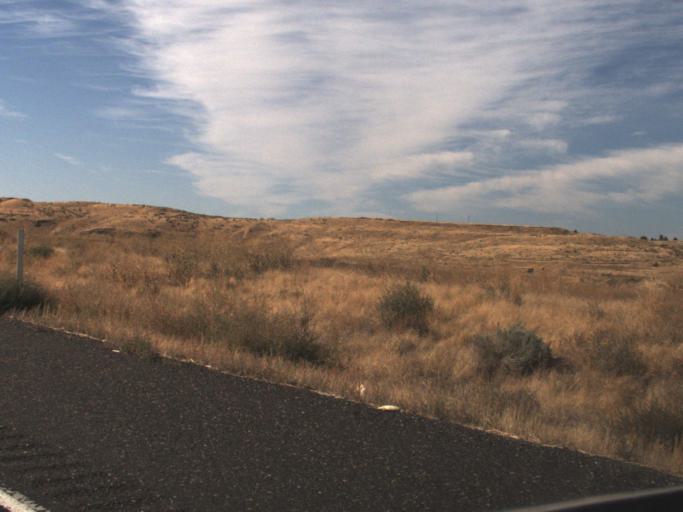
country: US
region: Washington
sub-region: Franklin County
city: Basin City
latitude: 46.5363
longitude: -119.0140
